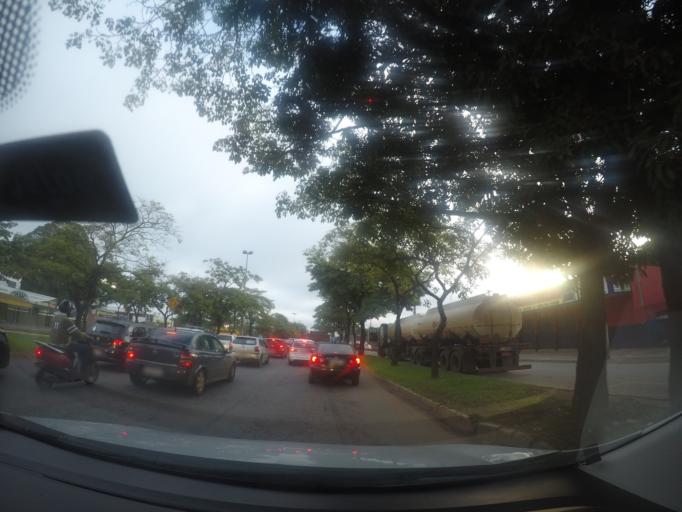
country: BR
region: Goias
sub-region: Goiania
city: Goiania
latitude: -16.6960
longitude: -49.3262
